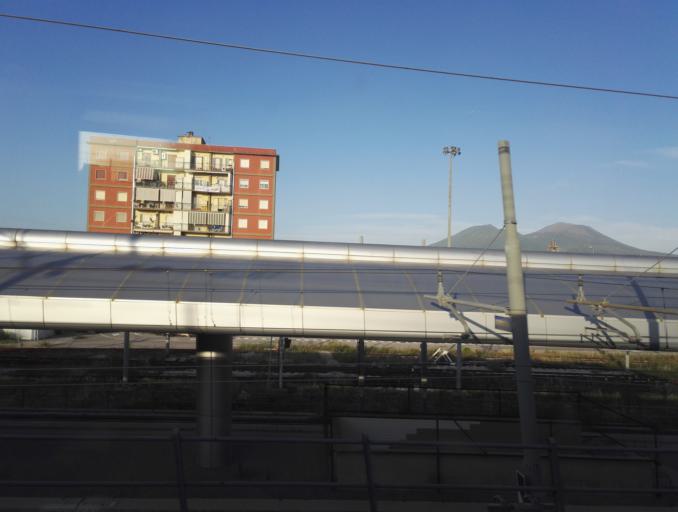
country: IT
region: Campania
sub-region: Provincia di Napoli
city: Arpino
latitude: 40.8582
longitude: 14.2973
